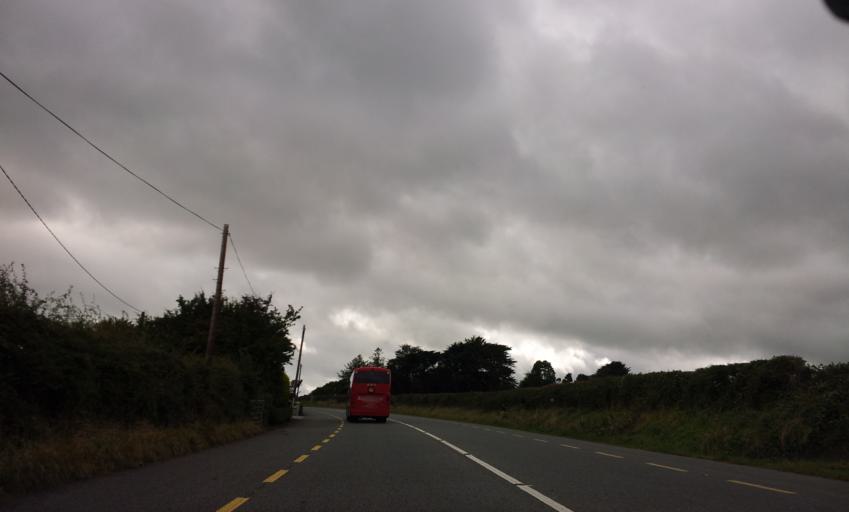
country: IE
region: Munster
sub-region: County Cork
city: Youghal
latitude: 51.9869
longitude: -7.7477
